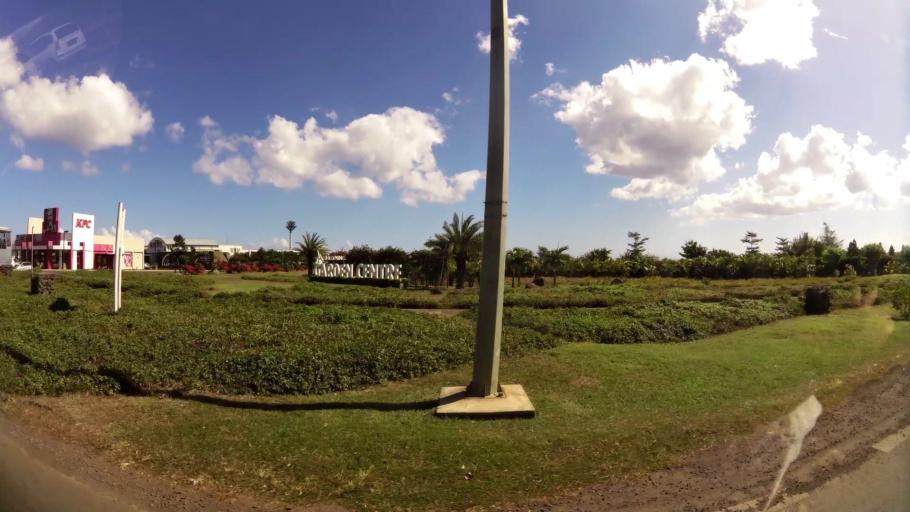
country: MU
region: Black River
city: Cascavelle
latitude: -20.2774
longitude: 57.4047
